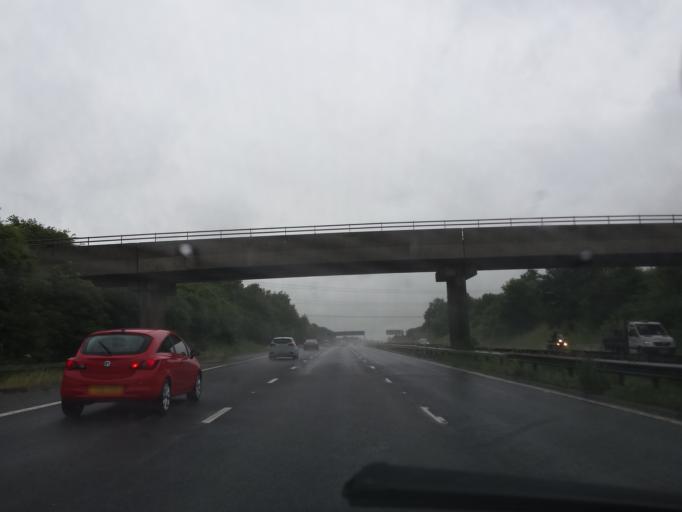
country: GB
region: England
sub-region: Rotherham
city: Bramley
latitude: 53.4072
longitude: -1.2598
